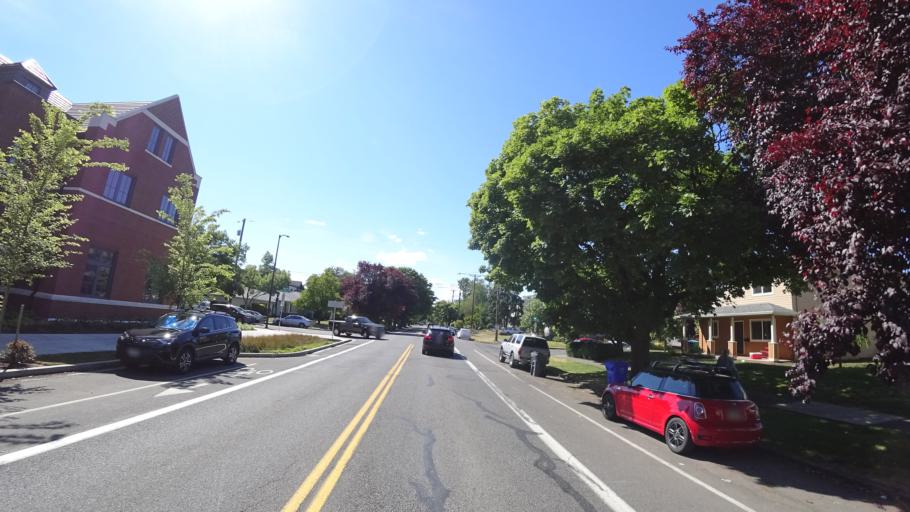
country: US
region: Oregon
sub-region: Washington County
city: West Haven
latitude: 45.5764
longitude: -122.7298
